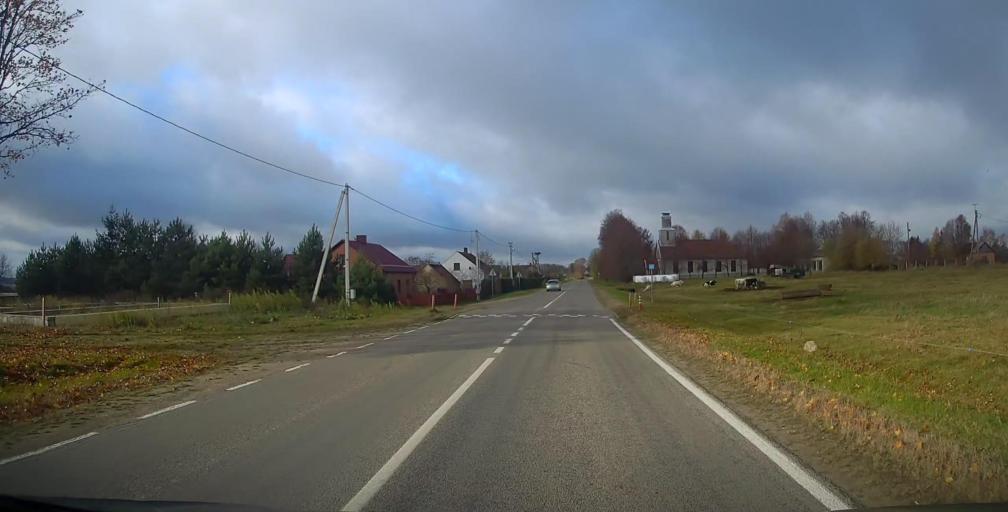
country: LT
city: Kybartai
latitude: 54.4548
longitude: 22.7331
